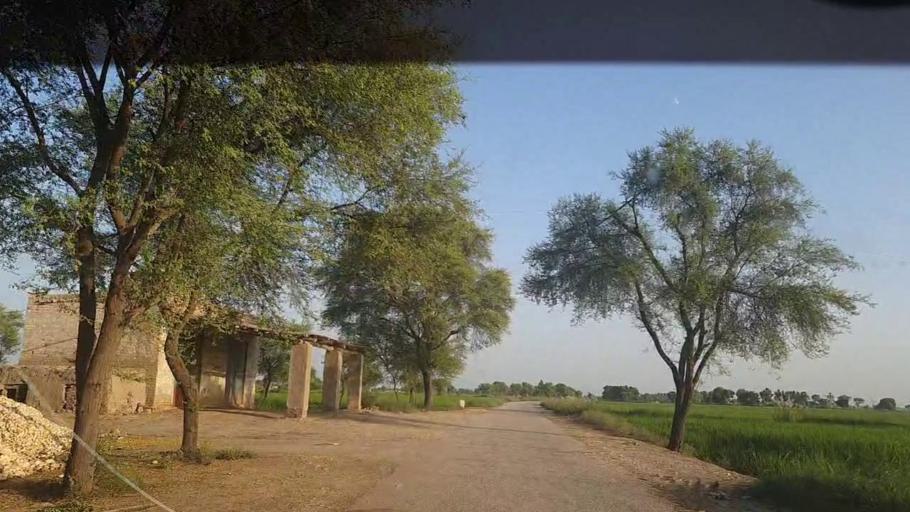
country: PK
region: Sindh
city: Thul
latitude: 28.1285
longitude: 68.8925
